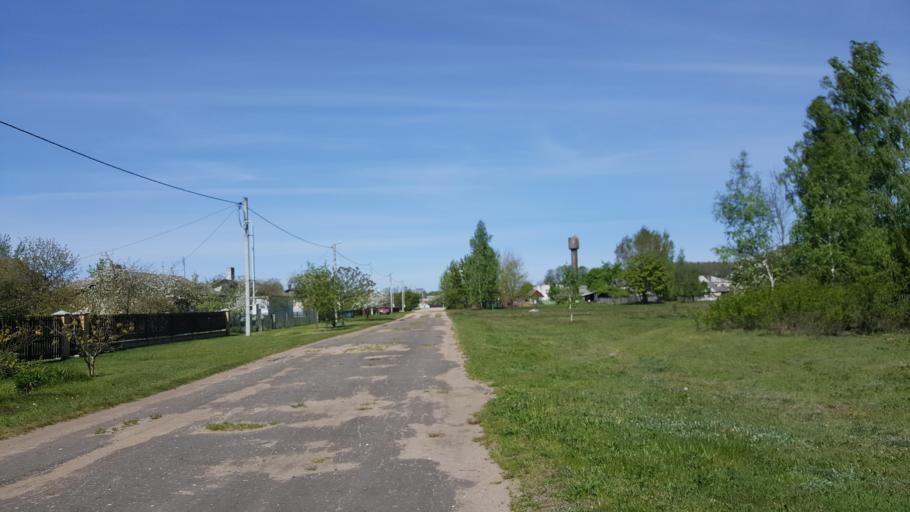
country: BY
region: Brest
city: Zhabinka
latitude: 52.3910
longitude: 24.0058
